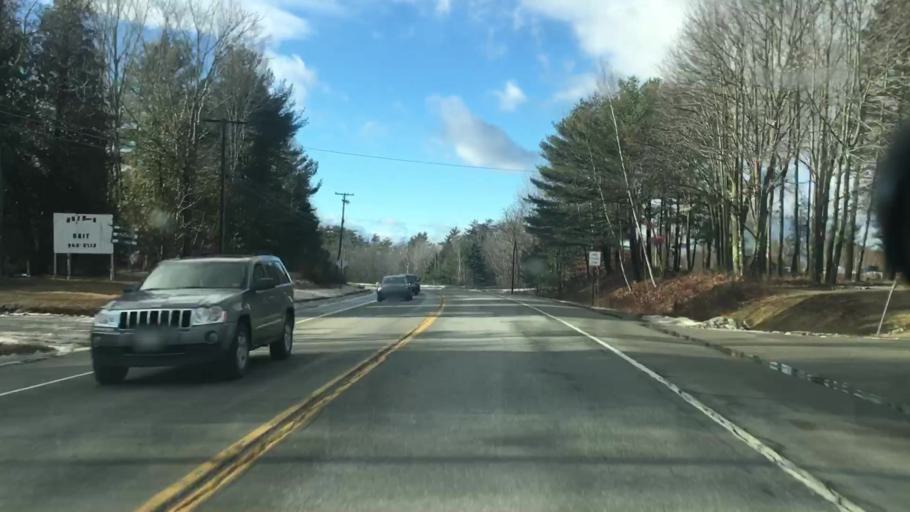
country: US
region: Maine
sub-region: Penobscot County
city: Holden
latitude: 44.7553
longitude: -68.6627
